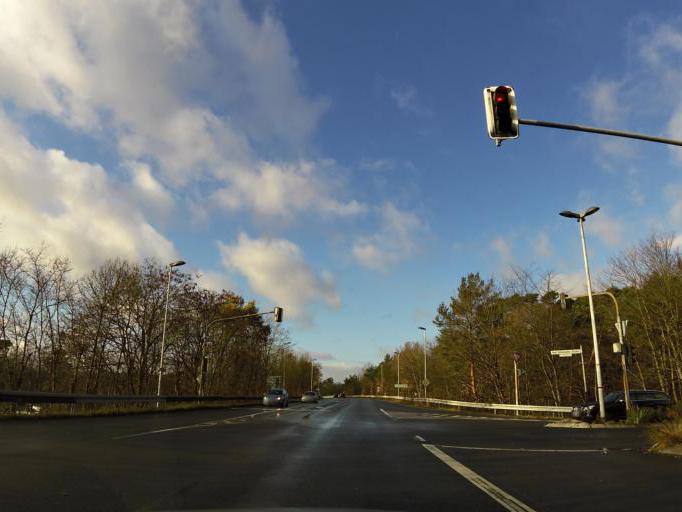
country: DE
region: Hesse
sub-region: Regierungsbezirk Darmstadt
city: Neu Isenburg
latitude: 50.0483
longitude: 8.6684
